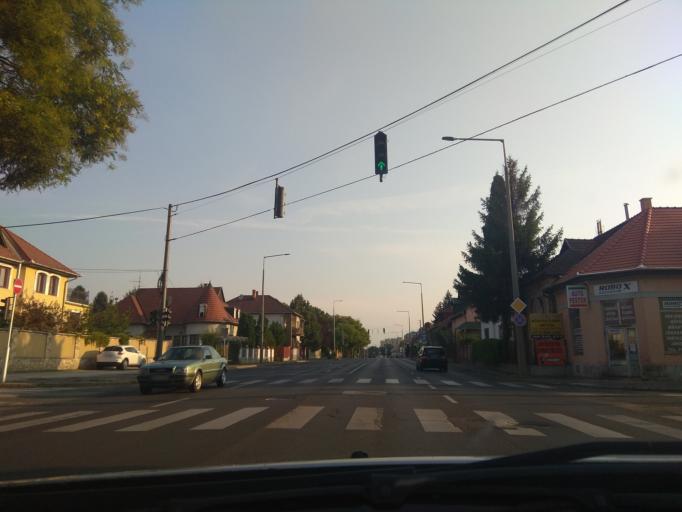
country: HU
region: Borsod-Abauj-Zemplen
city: Miskolc
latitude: 48.0926
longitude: 20.7923
